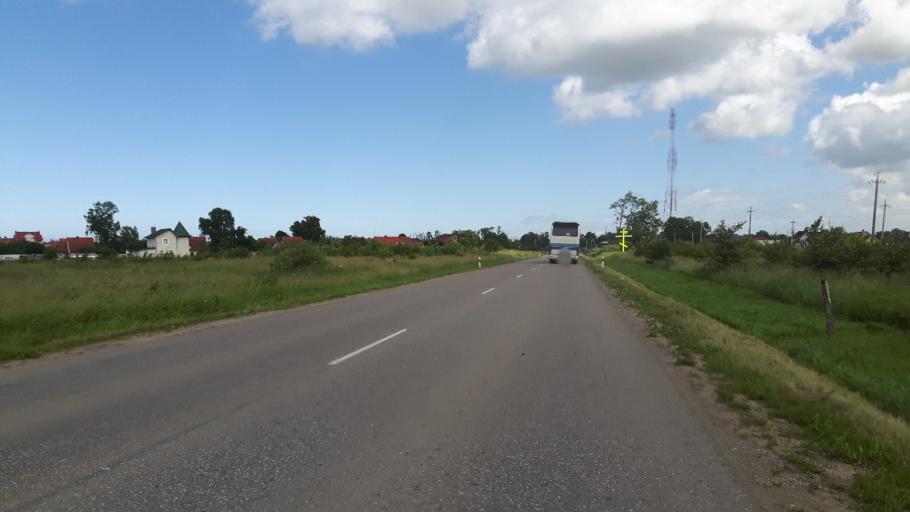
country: RU
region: Kaliningrad
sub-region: Zelenogradskiy Rayon
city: Zelenogradsk
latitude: 54.9417
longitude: 20.4596
